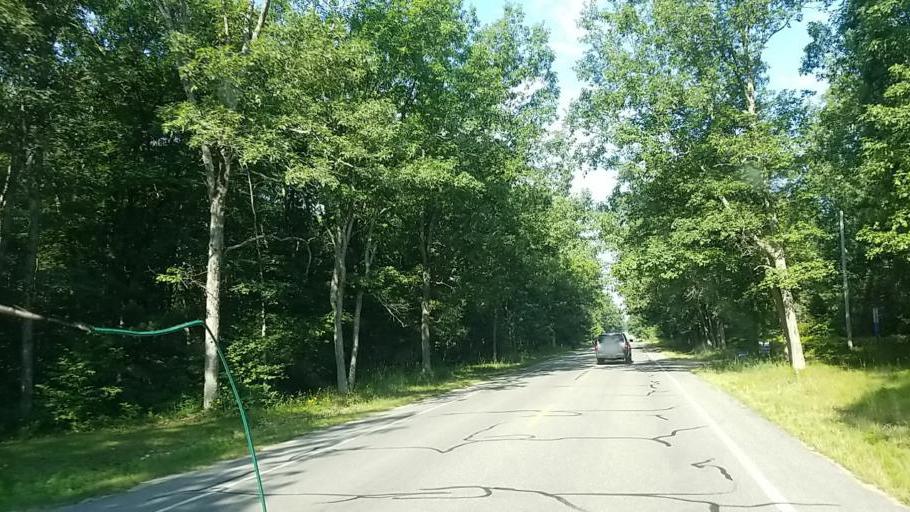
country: US
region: Michigan
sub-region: Muskegon County
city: Lakewood Club
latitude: 43.4695
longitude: -86.2450
